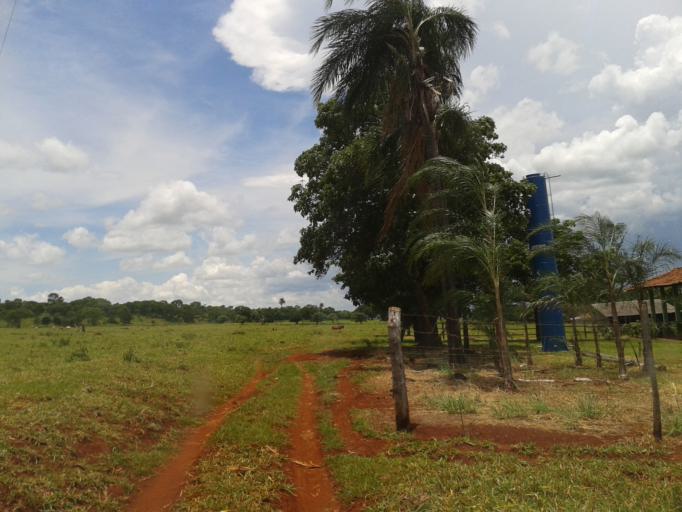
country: BR
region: Minas Gerais
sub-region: Centralina
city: Centralina
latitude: -18.7004
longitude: -49.2293
